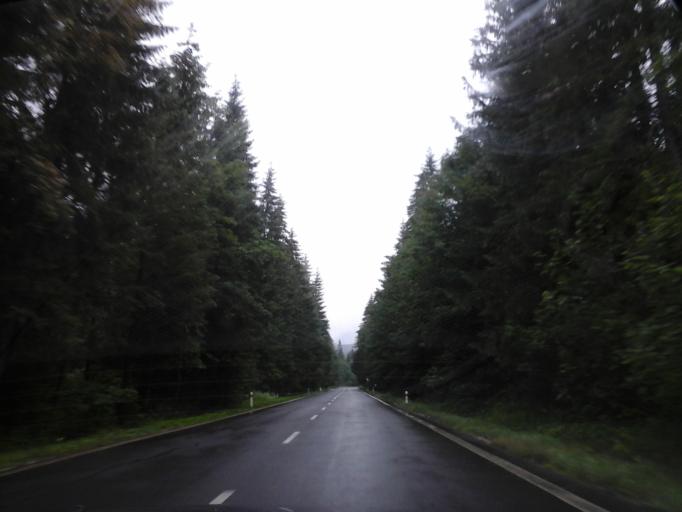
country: PL
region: Lesser Poland Voivodeship
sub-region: Powiat tatrzanski
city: Bukowina Tatrzanska
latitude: 49.2731
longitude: 20.1566
